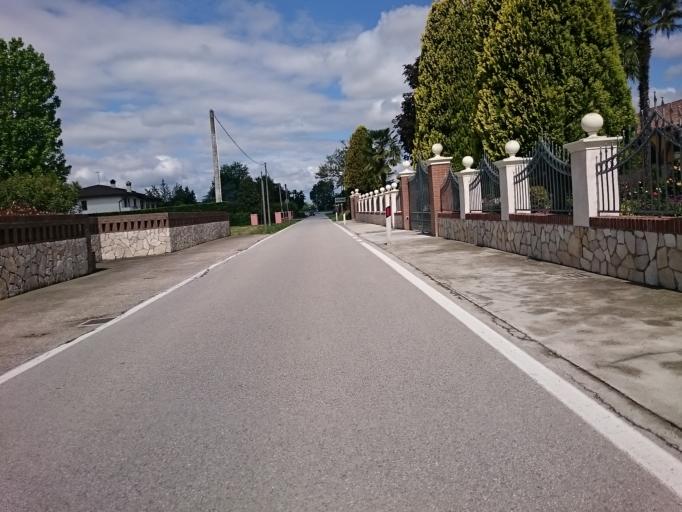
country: IT
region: Veneto
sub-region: Provincia di Padova
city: Mestrino
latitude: 45.4391
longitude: 11.7768
